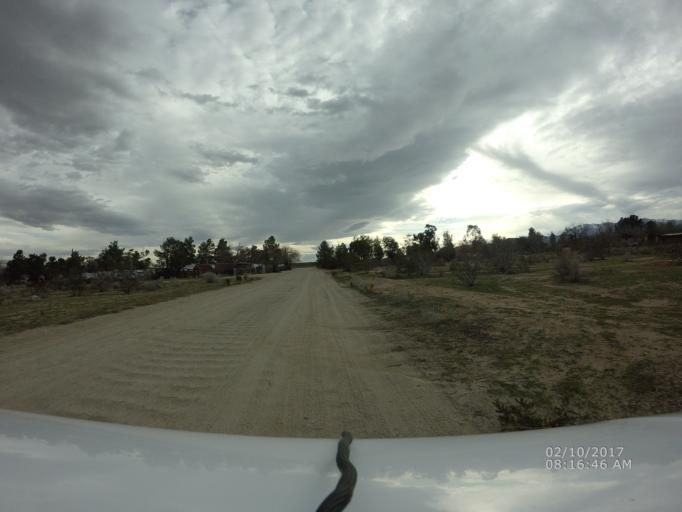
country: US
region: California
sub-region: Los Angeles County
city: Littlerock
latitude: 34.5046
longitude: -117.9031
